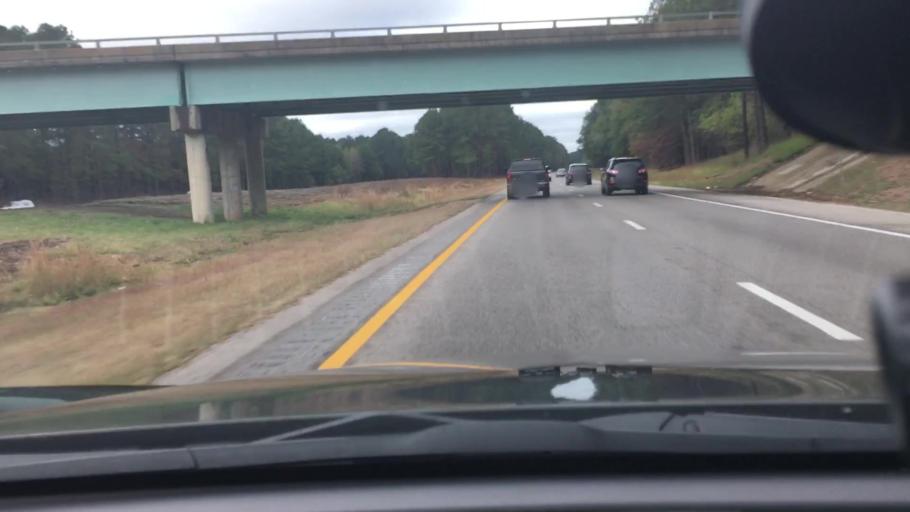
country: US
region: North Carolina
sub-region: Nash County
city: Spring Hope
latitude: 35.7898
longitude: -78.1378
